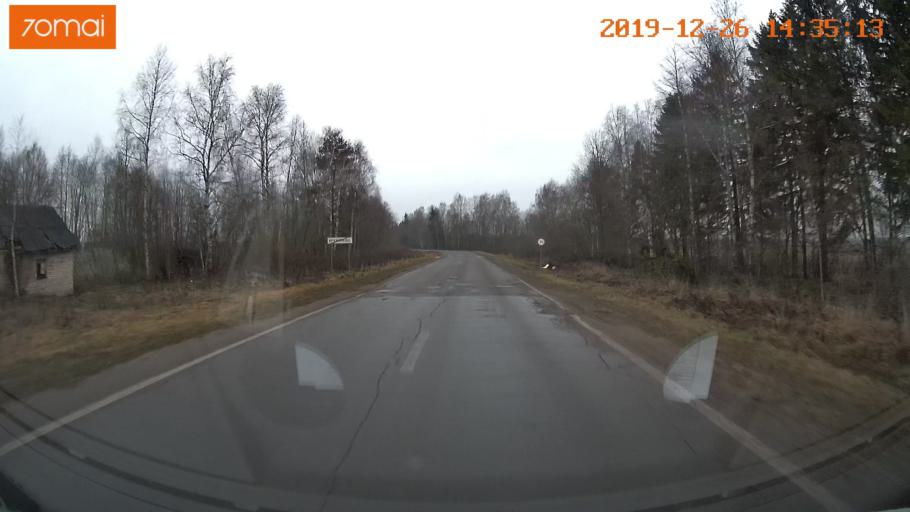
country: RU
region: Jaroslavl
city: Poshekhon'ye
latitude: 58.4220
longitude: 38.9879
